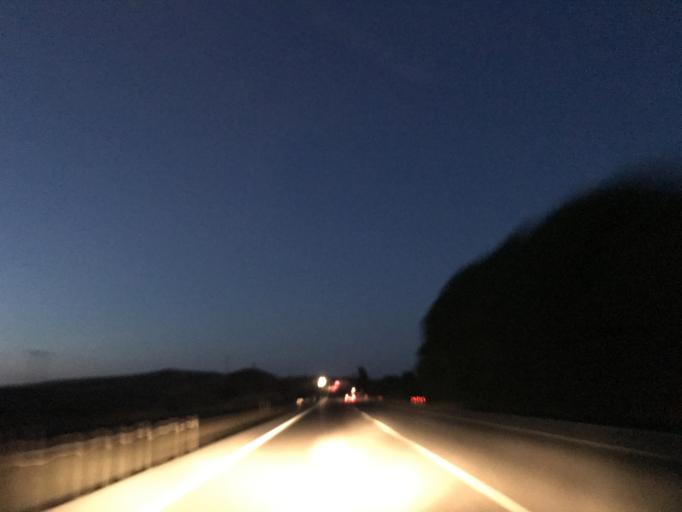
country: TR
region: Yozgat
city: Yerkoy
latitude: 39.6712
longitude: 34.5732
